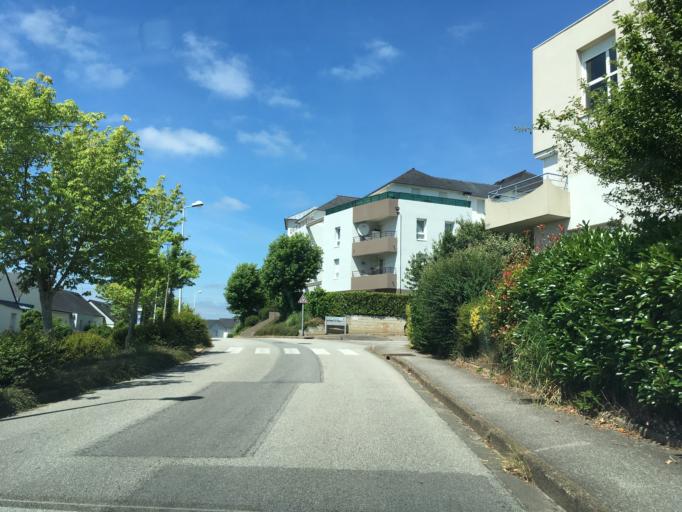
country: FR
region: Brittany
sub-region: Departement du Finistere
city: Quimper
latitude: 48.0067
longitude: -4.1007
